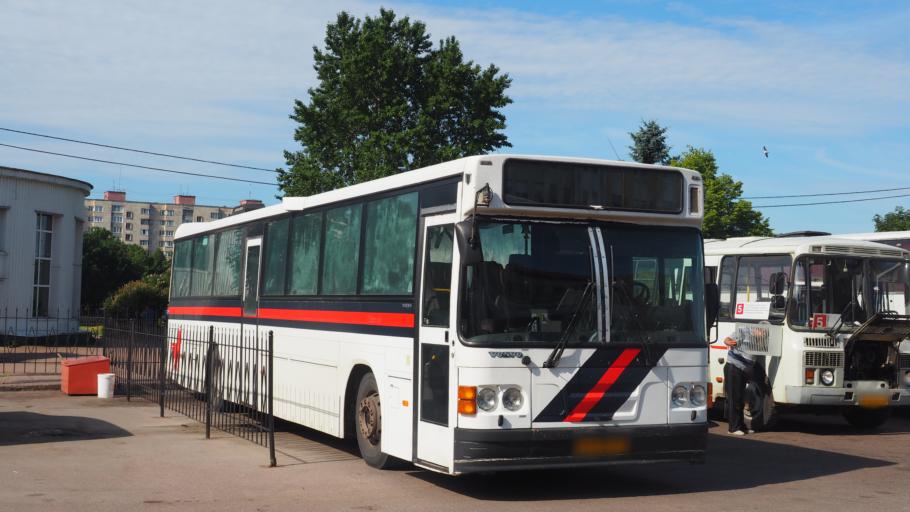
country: RU
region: Leningrad
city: Vyborg
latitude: 60.7148
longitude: 28.7488
